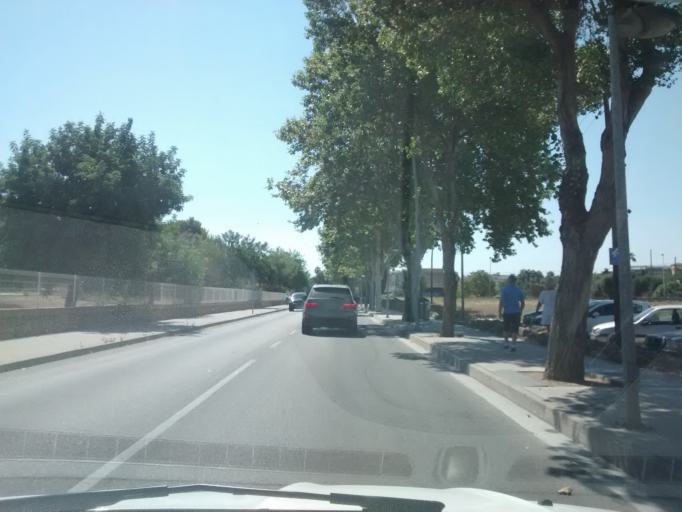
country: ES
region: Balearic Islands
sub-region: Illes Balears
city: Alcudia
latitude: 39.8489
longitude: 3.1282
